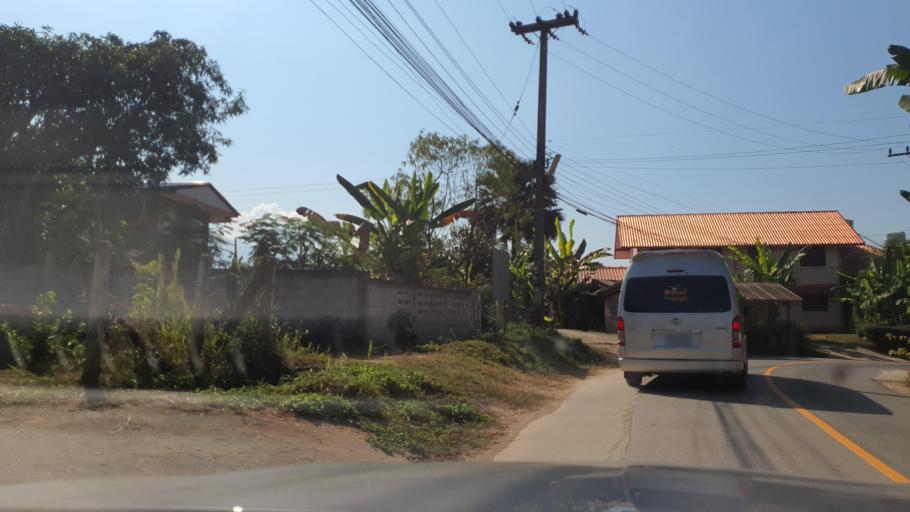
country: TH
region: Nan
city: Pua
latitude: 19.1640
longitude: 100.9295
